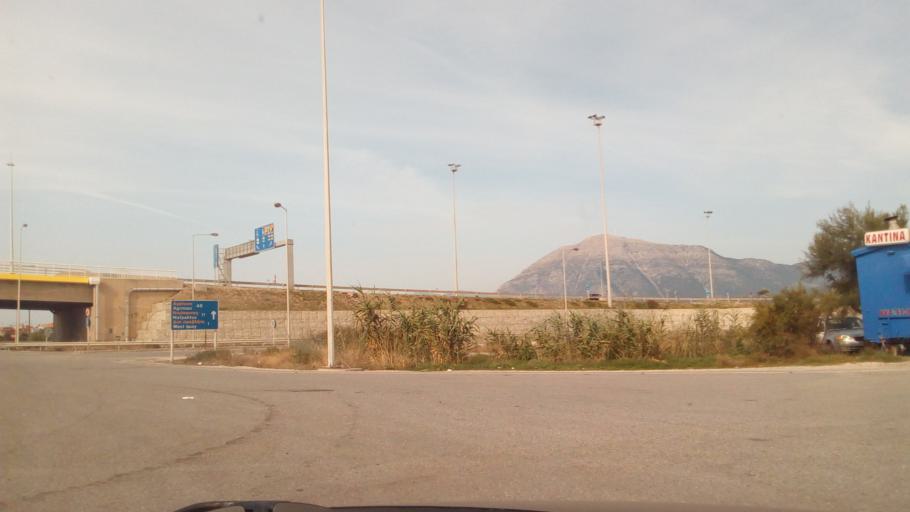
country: GR
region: West Greece
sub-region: Nomos Aitolias kai Akarnanias
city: Antirrio
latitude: 38.3319
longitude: 21.7683
